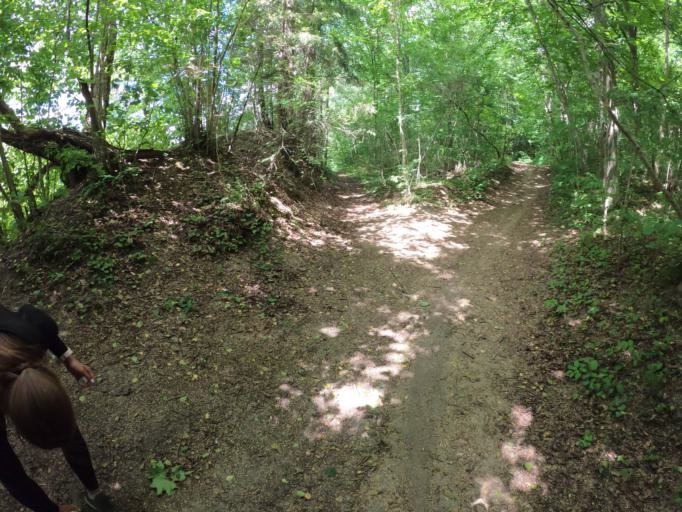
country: LT
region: Alytaus apskritis
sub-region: Alytus
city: Alytus
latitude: 54.3867
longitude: 24.0916
